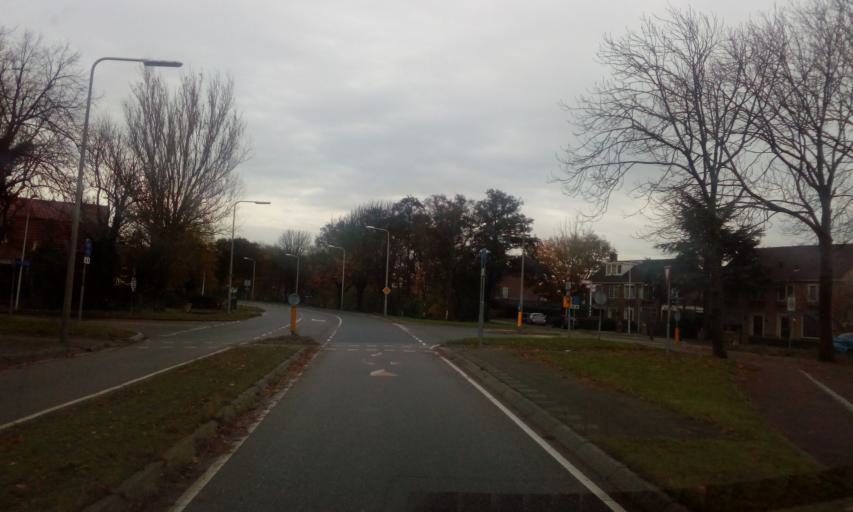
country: NL
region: South Holland
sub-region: Gemeente Westland
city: Kwintsheul
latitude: 52.0274
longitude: 4.2642
